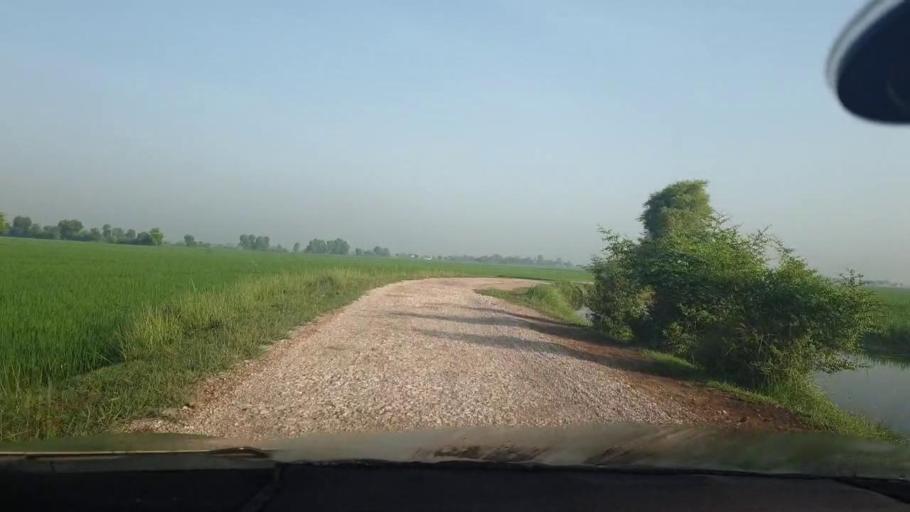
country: PK
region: Sindh
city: Kambar
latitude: 27.6213
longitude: 68.0179
